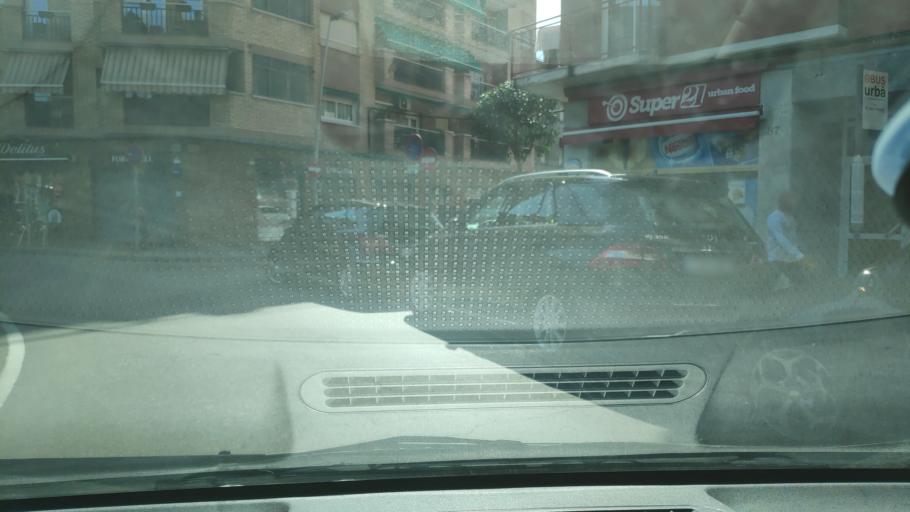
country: ES
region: Catalonia
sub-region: Provincia de Barcelona
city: Mollet del Valles
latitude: 41.5412
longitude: 2.2186
